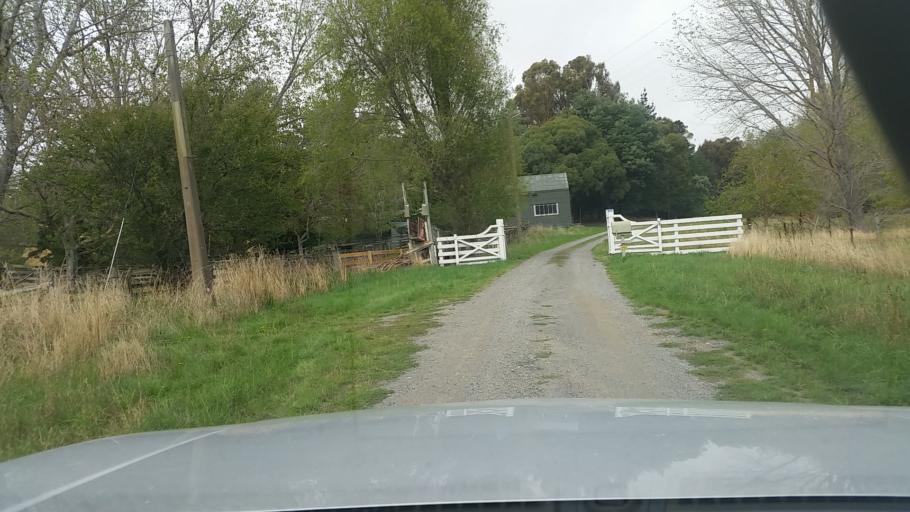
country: NZ
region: Marlborough
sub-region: Marlborough District
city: Blenheim
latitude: -41.7331
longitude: 173.9227
